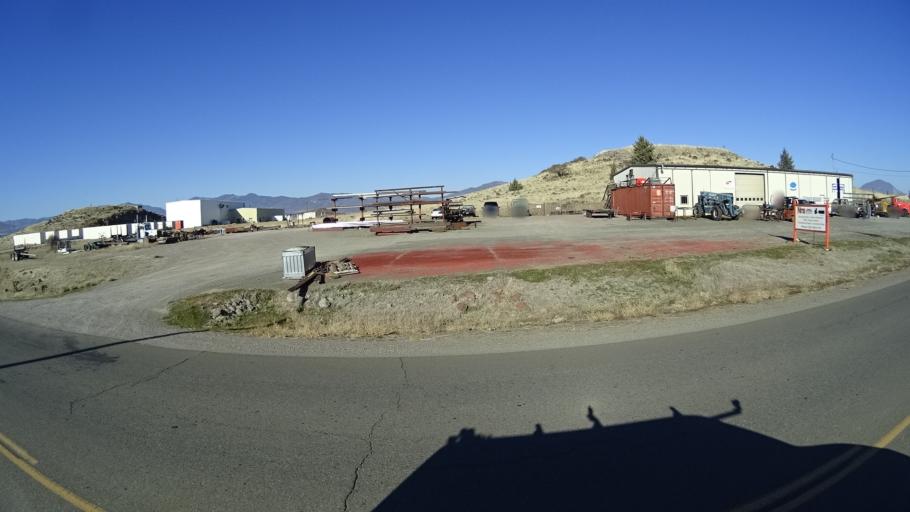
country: US
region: California
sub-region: Siskiyou County
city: Montague
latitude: 41.7226
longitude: -122.5318
